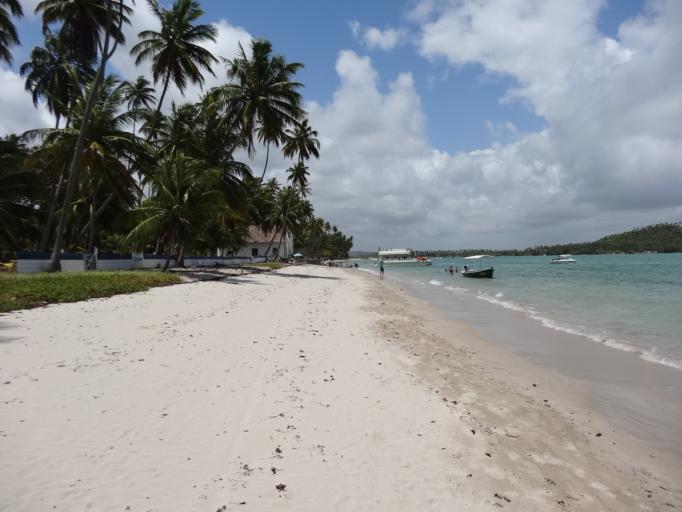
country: BR
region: Pernambuco
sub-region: Tamandare
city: Tamandare
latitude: -8.6960
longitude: -35.0896
